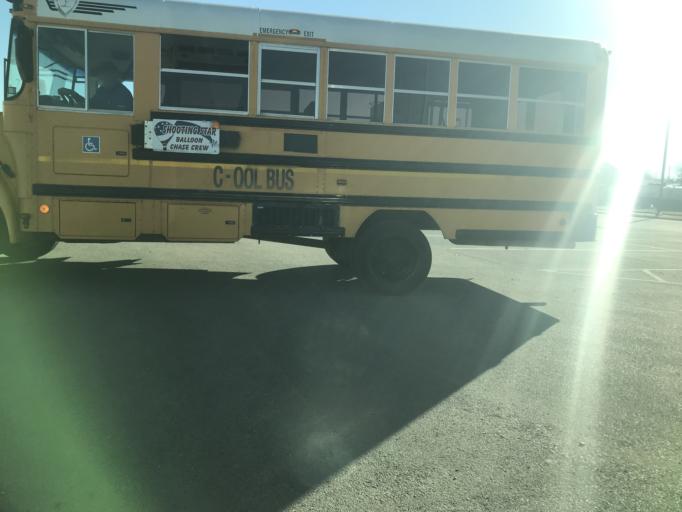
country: US
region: Texas
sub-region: Taylor County
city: Abilene
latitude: 32.4398
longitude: -99.7565
